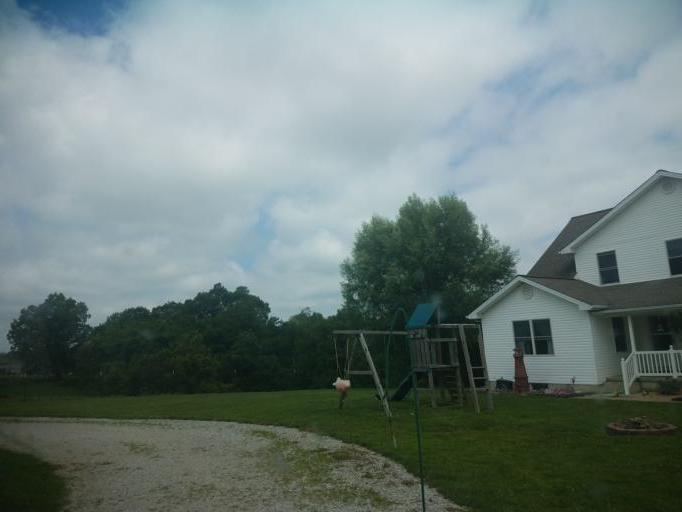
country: US
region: Kentucky
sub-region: Hart County
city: Munfordville
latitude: 37.3024
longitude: -85.9571
